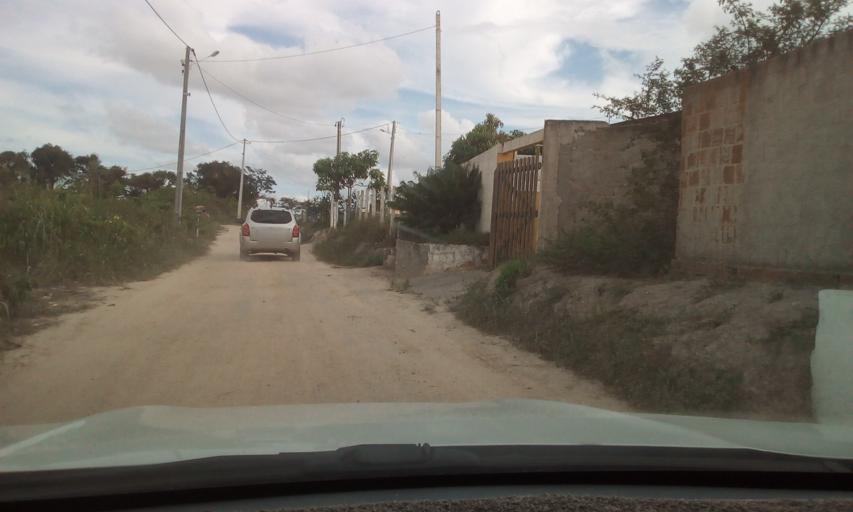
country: BR
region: Pernambuco
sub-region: Cha Grande
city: Cha Grande
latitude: -8.1922
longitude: -35.4971
